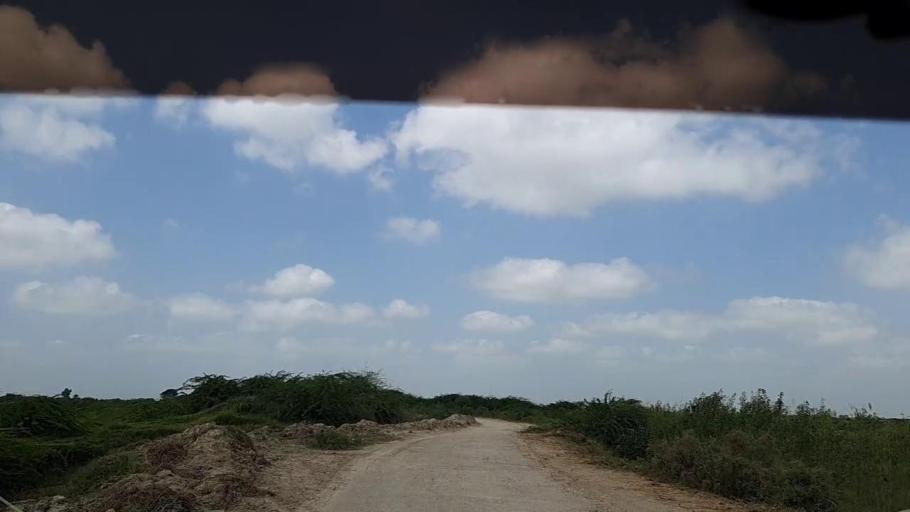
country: PK
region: Sindh
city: Badin
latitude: 24.5987
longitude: 68.7930
